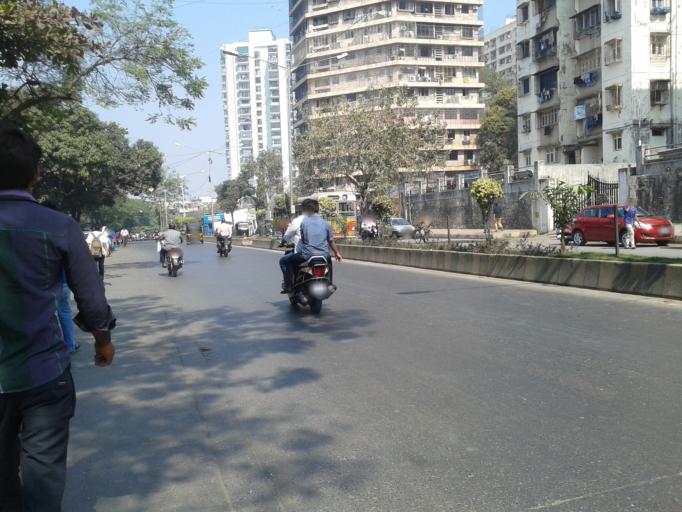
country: IN
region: Maharashtra
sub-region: Mumbai Suburban
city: Borivli
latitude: 19.2501
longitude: 72.8632
